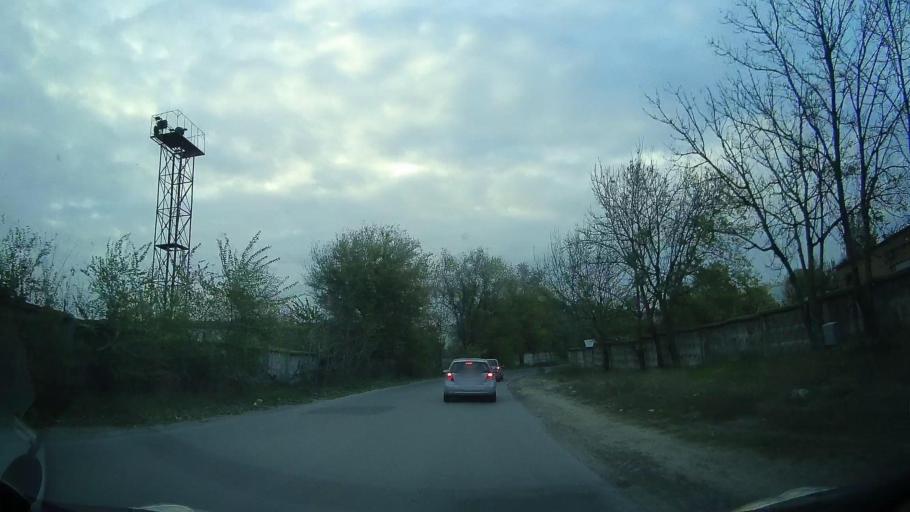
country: RU
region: Rostov
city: Severnyy
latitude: 47.2638
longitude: 39.6464
